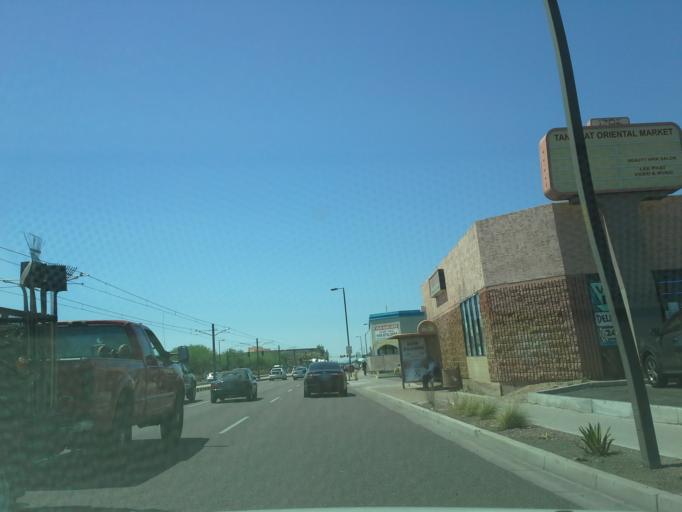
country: US
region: Arizona
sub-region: Maricopa County
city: Phoenix
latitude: 33.5097
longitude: -112.0959
